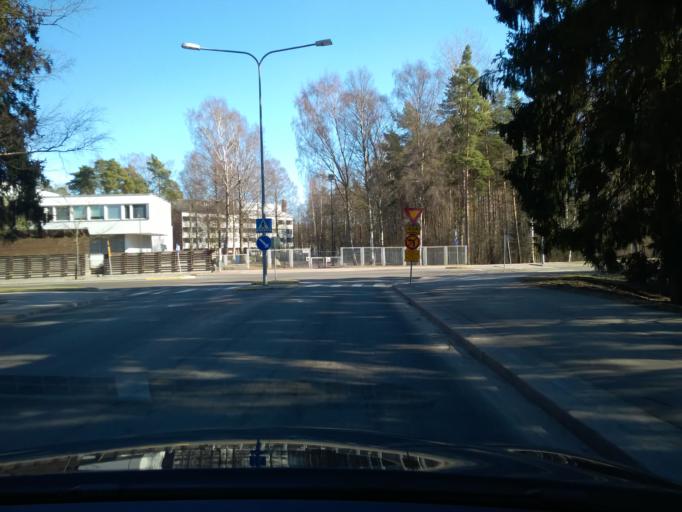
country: FI
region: Uusimaa
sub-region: Helsinki
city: Teekkarikylae
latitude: 60.2167
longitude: 24.8893
